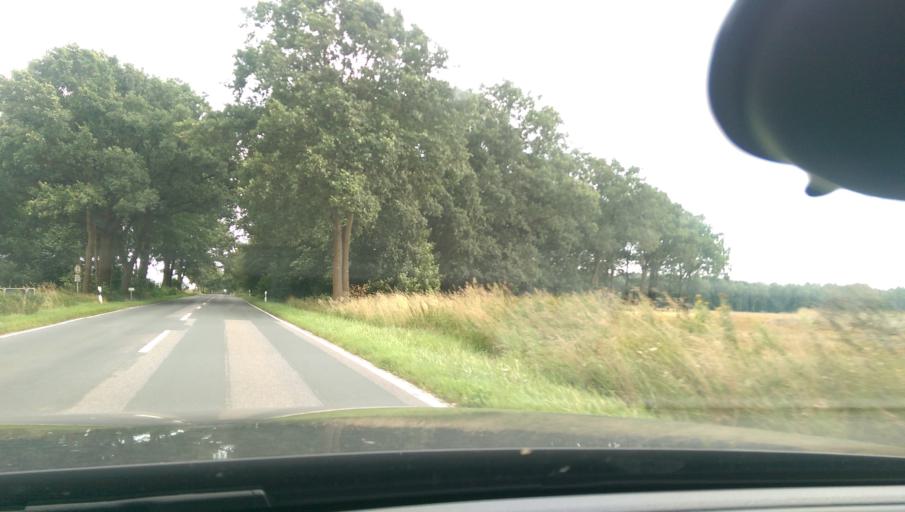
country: DE
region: Lower Saxony
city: Lindwedel
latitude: 52.5650
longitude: 9.6236
